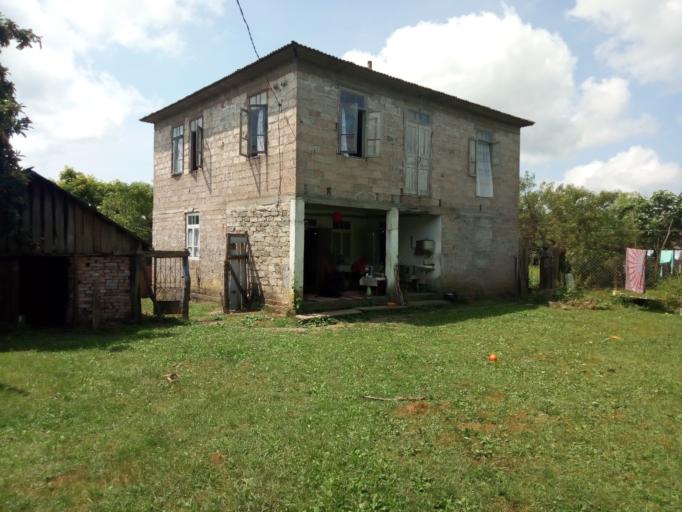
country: GE
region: Abkhazia
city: Dranda
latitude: 42.8803
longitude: 41.3332
